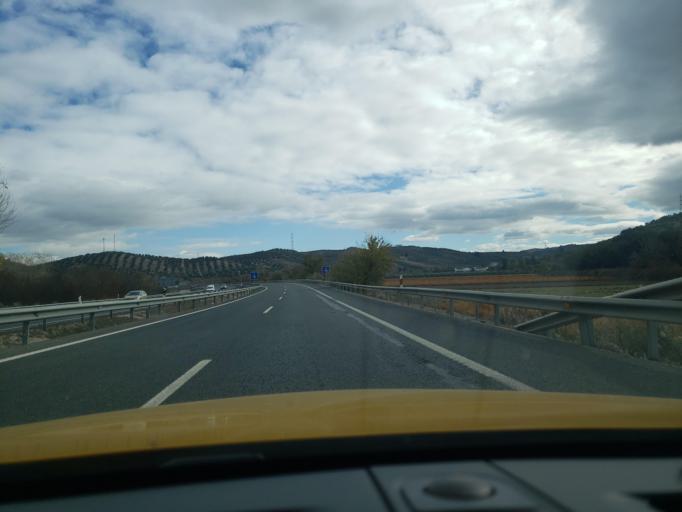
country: ES
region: Andalusia
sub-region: Provincia de Granada
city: Villanueva de Mesia
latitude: 37.1940
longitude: -4.0068
